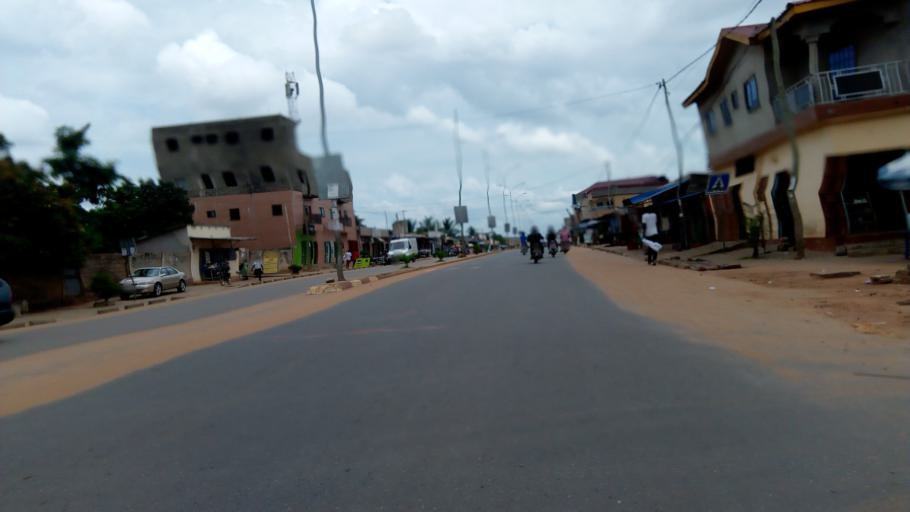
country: TG
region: Maritime
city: Lome
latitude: 6.2133
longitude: 1.1751
